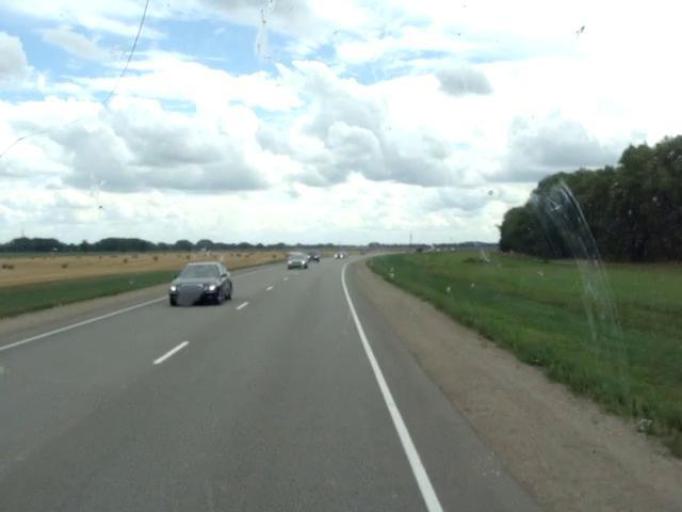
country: RU
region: Altai Krai
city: Shubenka
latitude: 52.6842
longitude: 85.0436
